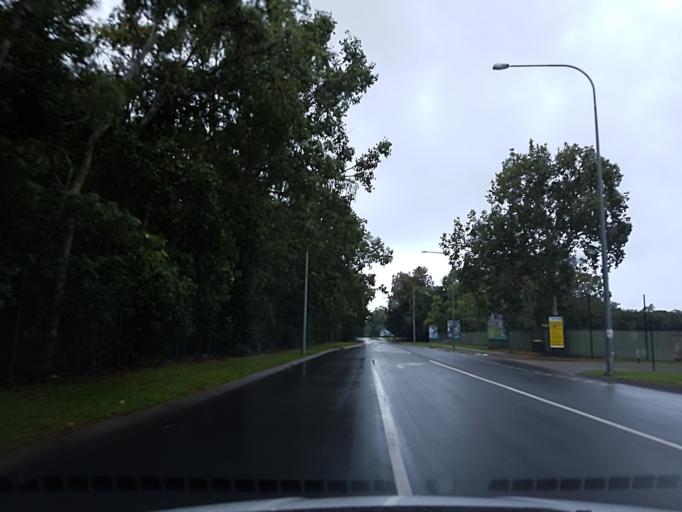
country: AU
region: Queensland
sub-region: Cairns
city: Palm Cove
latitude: -16.7538
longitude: 145.6664
